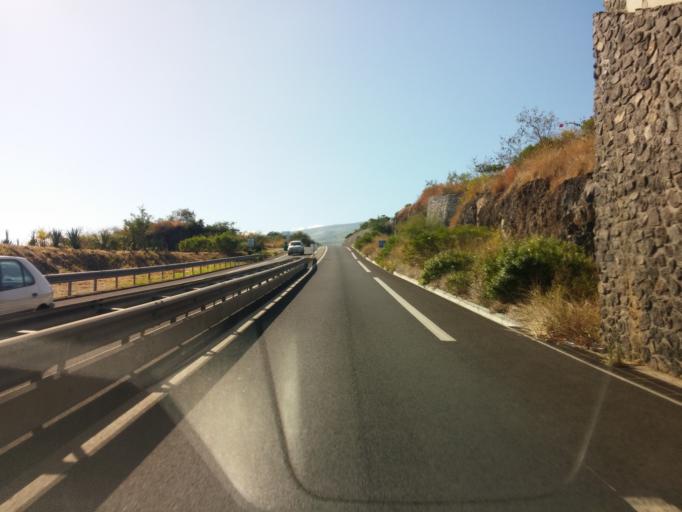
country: RE
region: Reunion
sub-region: Reunion
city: Saint-Paul
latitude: -21.0191
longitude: 55.2654
